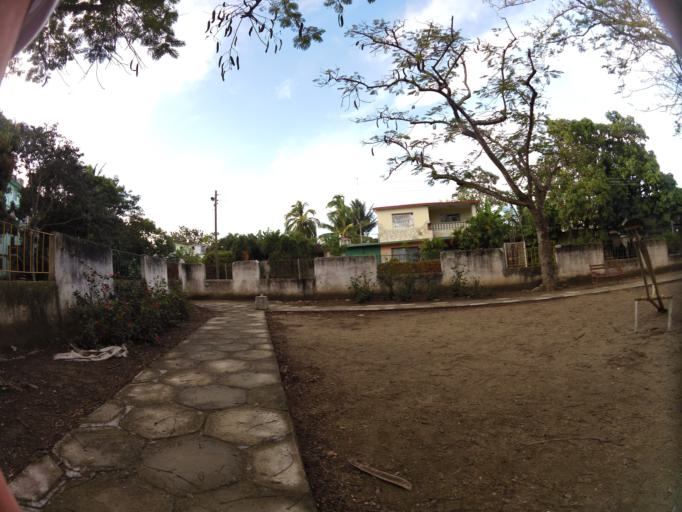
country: CU
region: Las Tunas
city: Las Tunas
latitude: 20.9684
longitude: -76.9328
